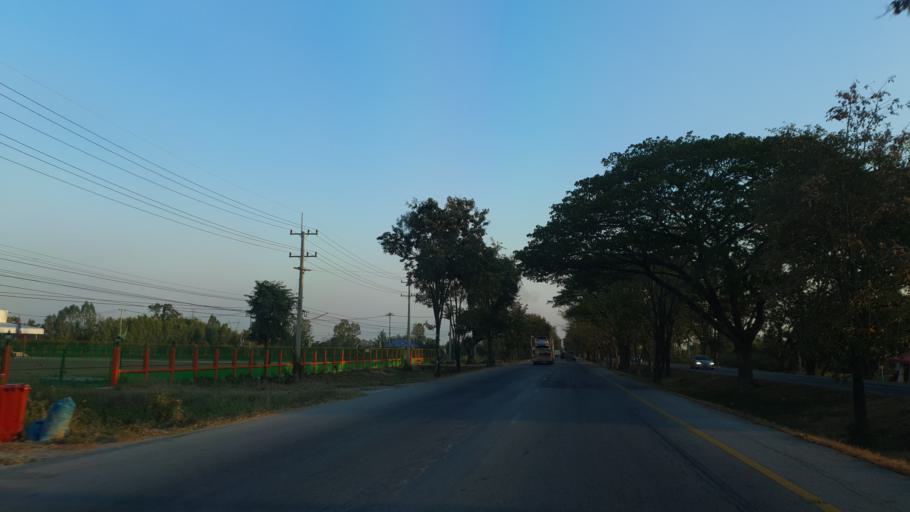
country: TH
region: Nakhon Sawan
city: Banphot Phisai
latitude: 15.9003
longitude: 99.8948
